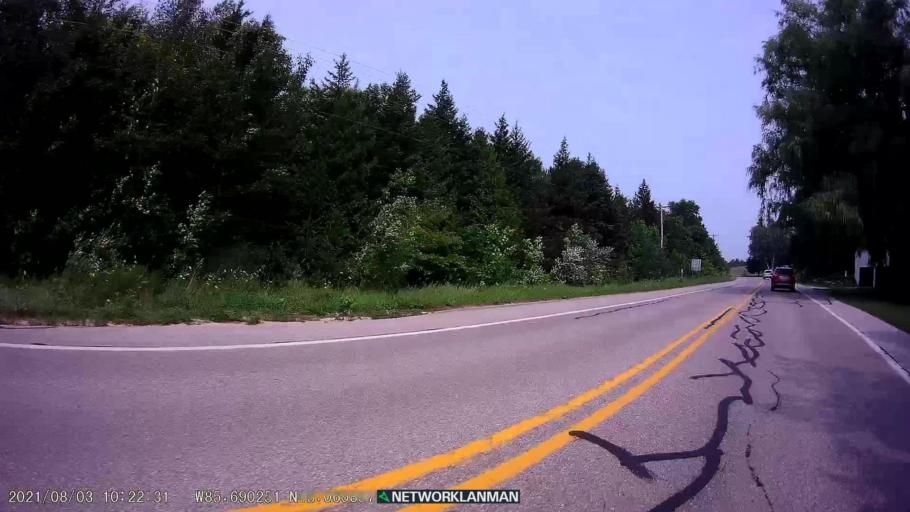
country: US
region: Michigan
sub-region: Leelanau County
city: Leland
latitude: 45.0699
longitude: -85.6902
